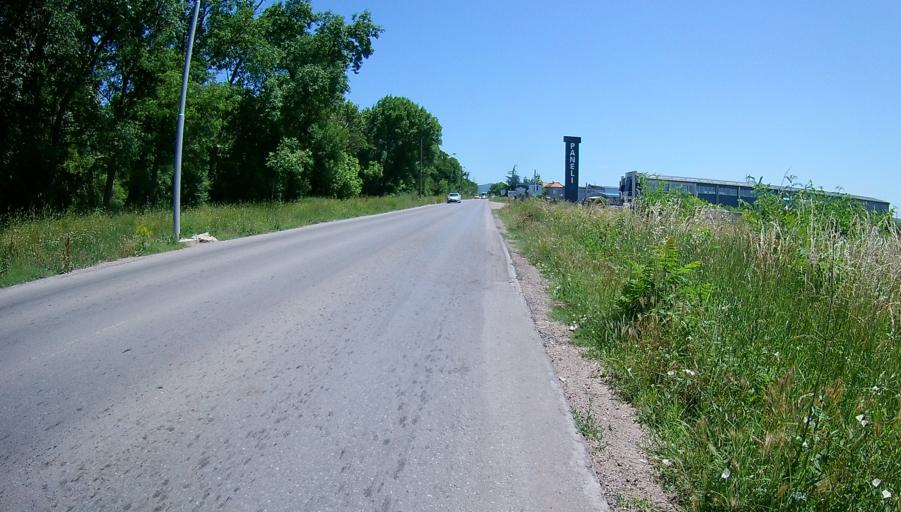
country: RS
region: Central Serbia
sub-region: Nisavski Okrug
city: Nis
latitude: 43.3017
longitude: 21.8728
